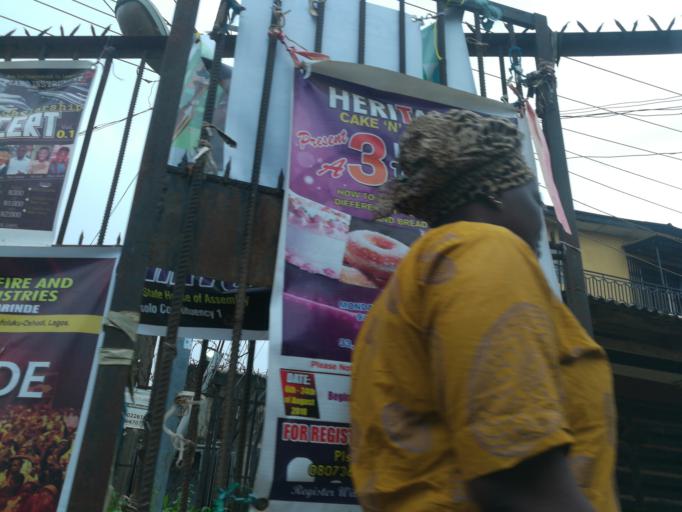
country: NG
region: Lagos
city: Oshodi
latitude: 6.5667
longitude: 3.3399
